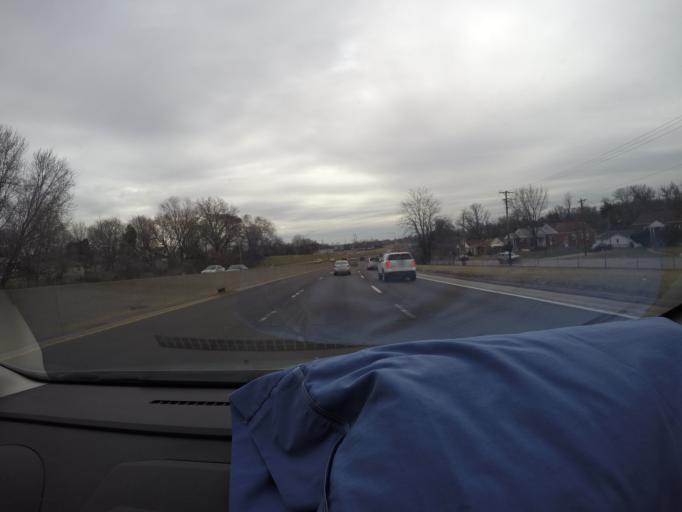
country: US
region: Missouri
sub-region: Saint Louis County
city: Northwoods
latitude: 38.7062
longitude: -90.2732
